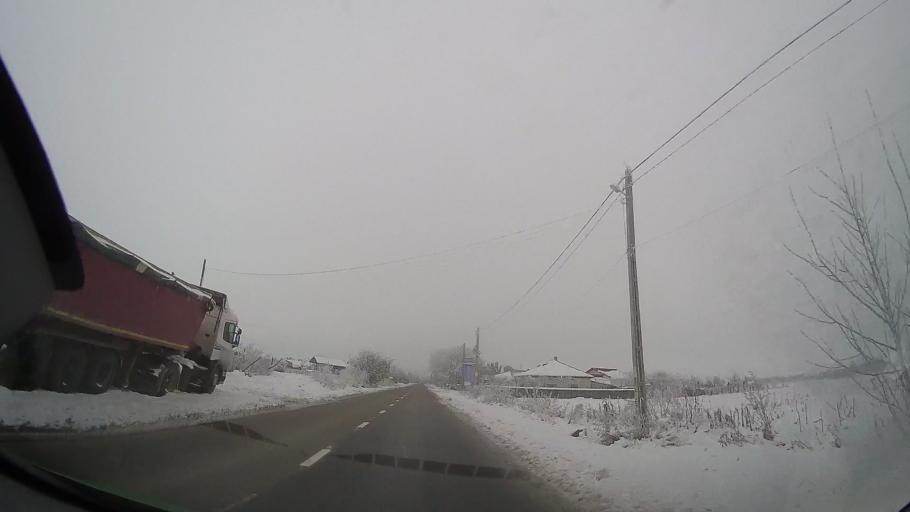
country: RO
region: Neamt
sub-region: Comuna Horia
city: Cotu Vames
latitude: 46.8955
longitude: 26.9603
